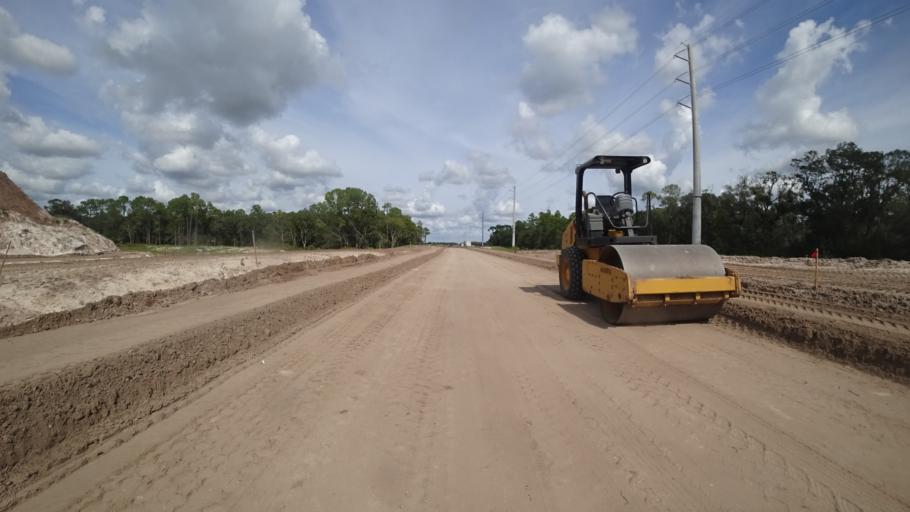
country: US
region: Florida
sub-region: Sarasota County
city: The Meadows
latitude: 27.4238
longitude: -82.3522
